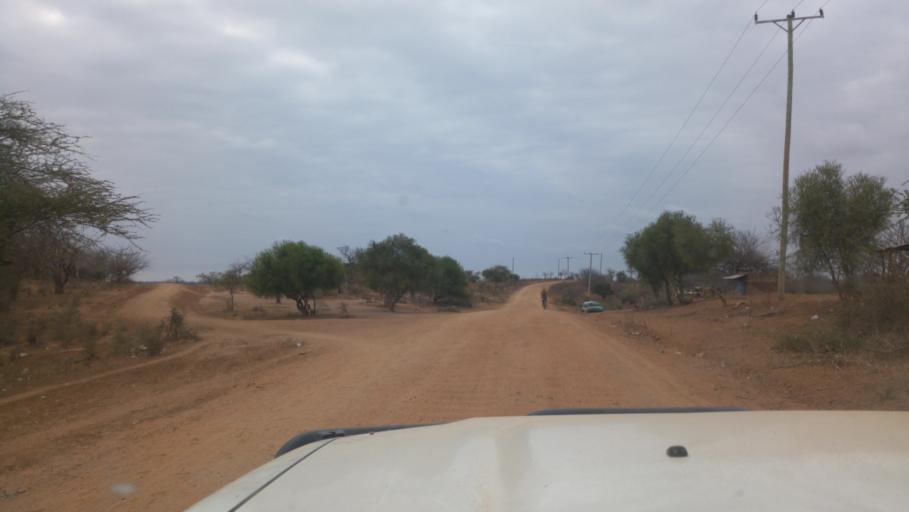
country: KE
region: Makueni
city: Makueni
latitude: -1.9696
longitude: 38.0952
